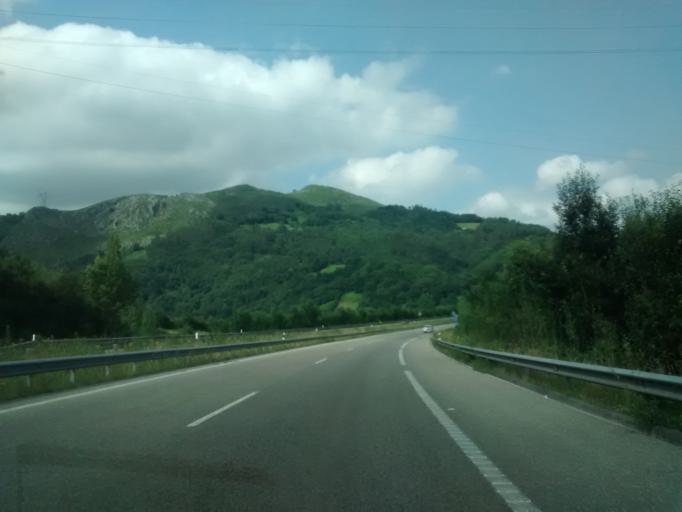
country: ES
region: Asturias
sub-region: Province of Asturias
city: Sama
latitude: 43.3191
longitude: -5.7446
